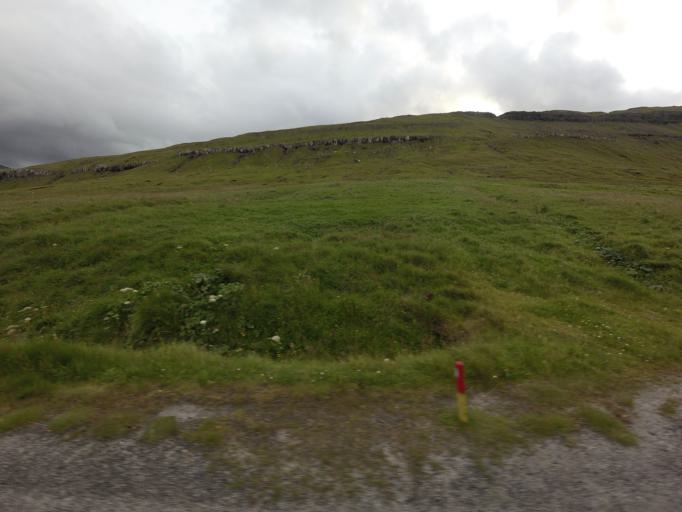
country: FO
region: Streymoy
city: Kollafjordhur
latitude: 62.1289
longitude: -6.8780
